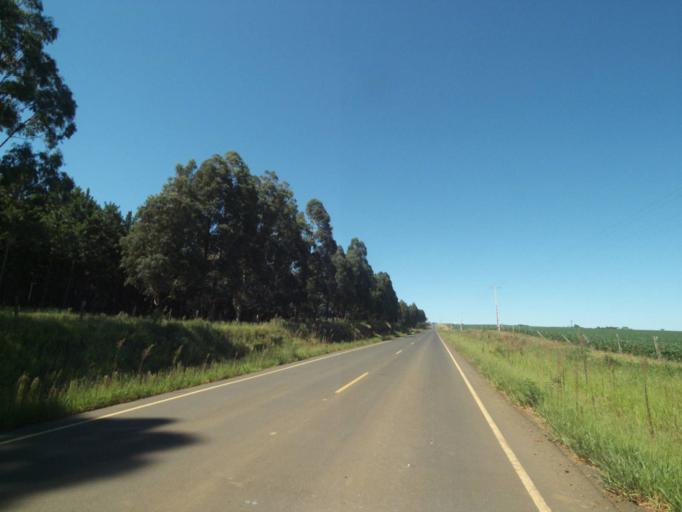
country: BR
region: Parana
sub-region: Pinhao
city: Pinhao
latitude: -25.8270
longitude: -52.0174
